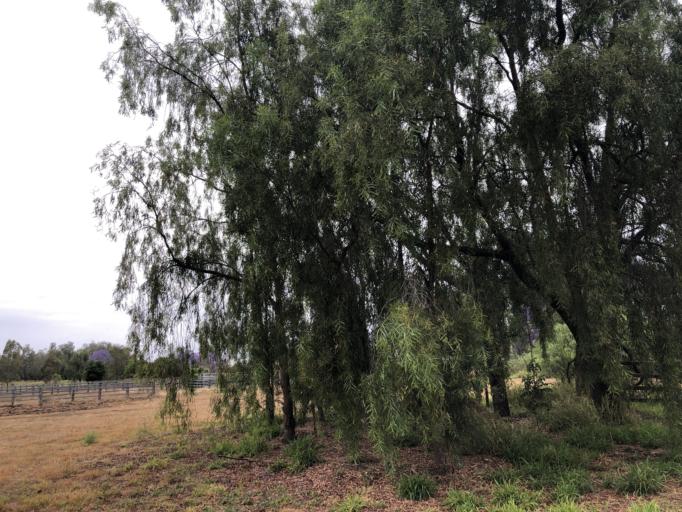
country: AU
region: Queensland
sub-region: Lockyer Valley
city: Gatton
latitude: -27.5867
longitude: 152.3440
